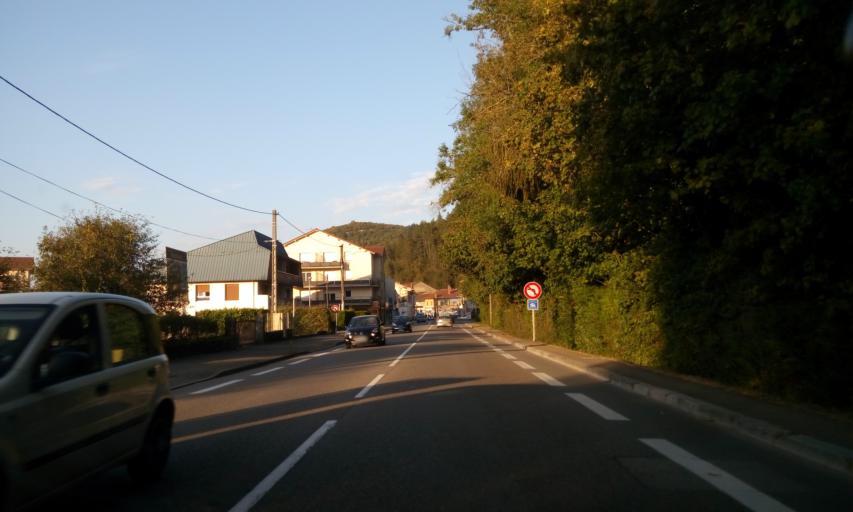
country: FR
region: Rhone-Alpes
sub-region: Departement de l'Ain
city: Montreal-la-Cluse
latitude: 46.1694
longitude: 5.5734
